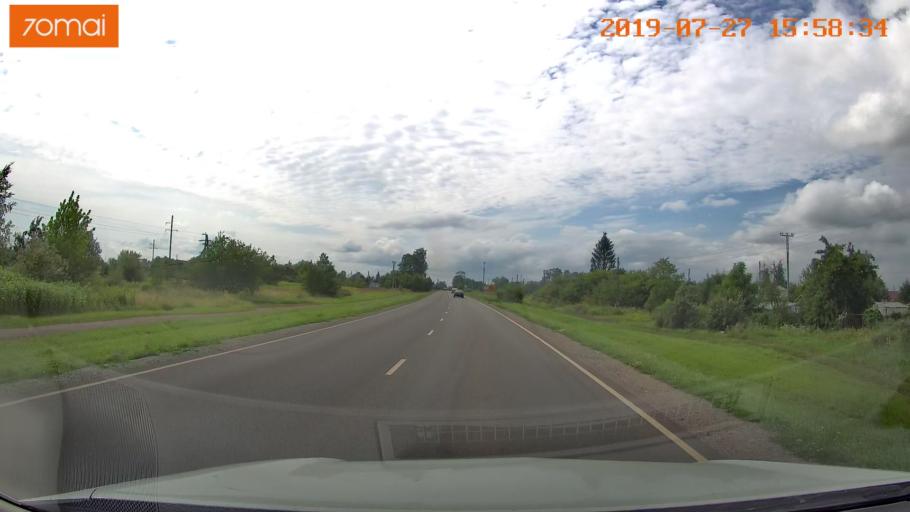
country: RU
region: Kaliningrad
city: Chernyakhovsk
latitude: 54.6263
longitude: 21.8620
